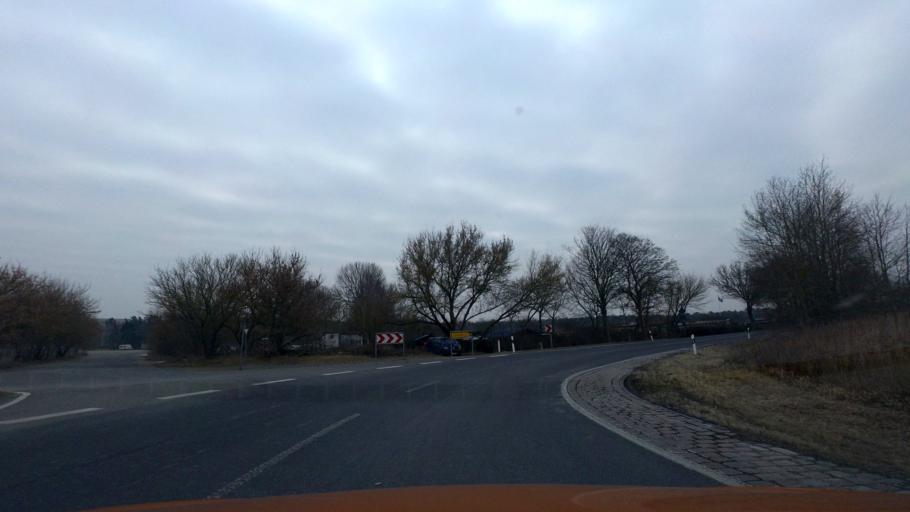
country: DE
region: Brandenburg
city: Ludwigsfelde
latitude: 52.3295
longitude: 13.2542
